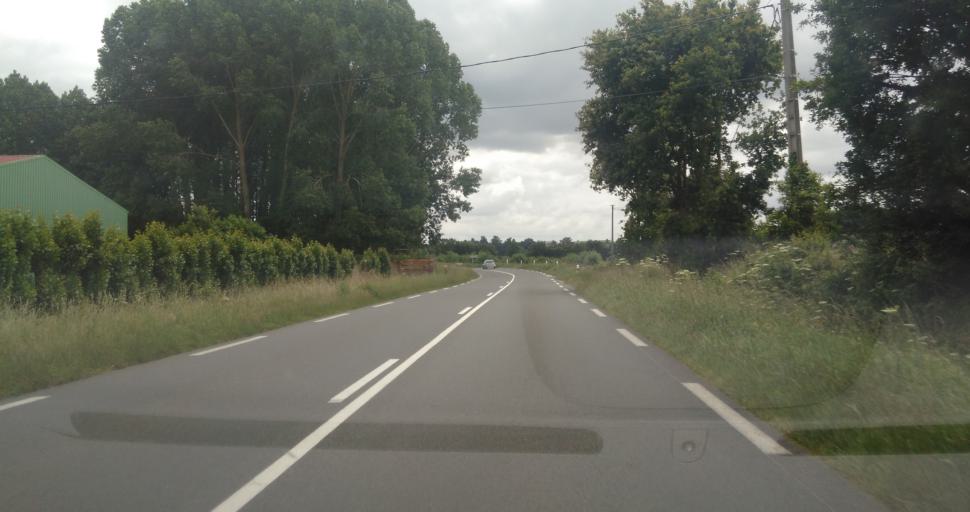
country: FR
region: Pays de la Loire
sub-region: Departement de la Vendee
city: Sainte-Hermine
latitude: 46.5793
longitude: -1.1085
